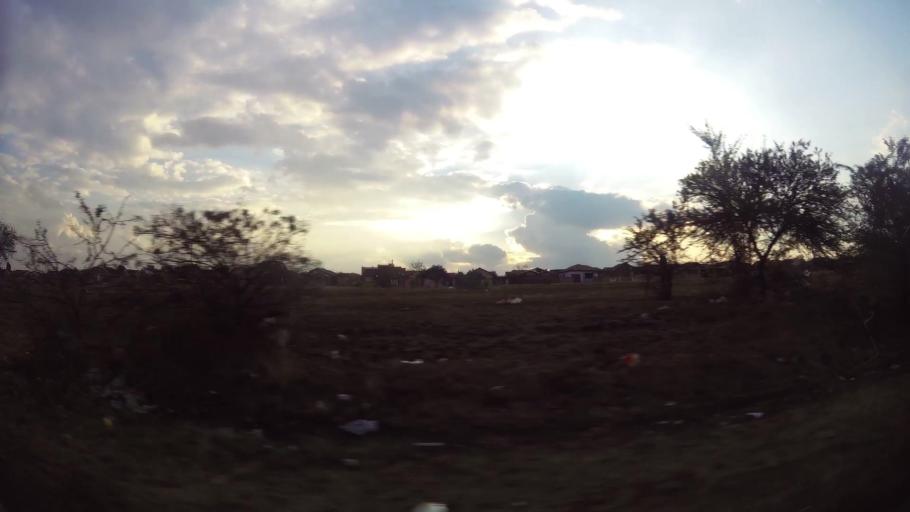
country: ZA
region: Gauteng
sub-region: City of Johannesburg Metropolitan Municipality
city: Orange Farm
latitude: -26.5845
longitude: 27.8546
